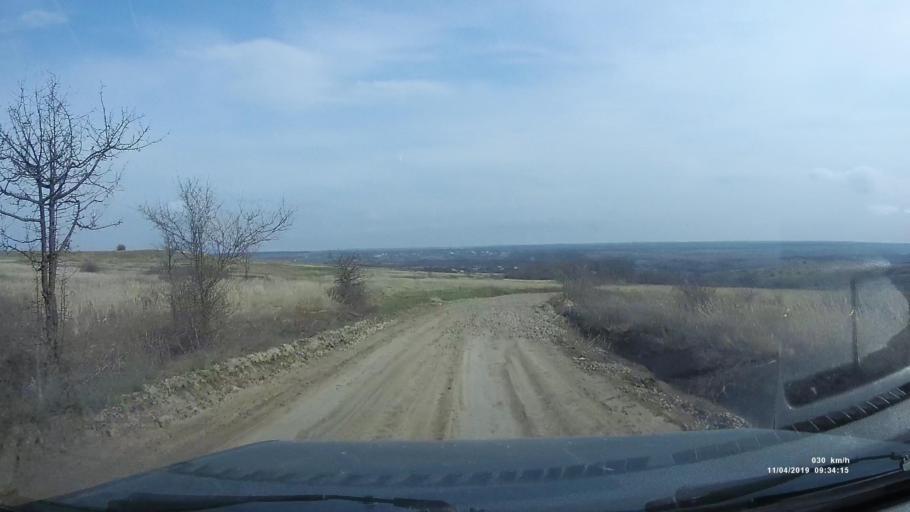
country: RU
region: Rostov
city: Staraya Stanitsa
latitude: 48.2685
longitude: 40.3691
